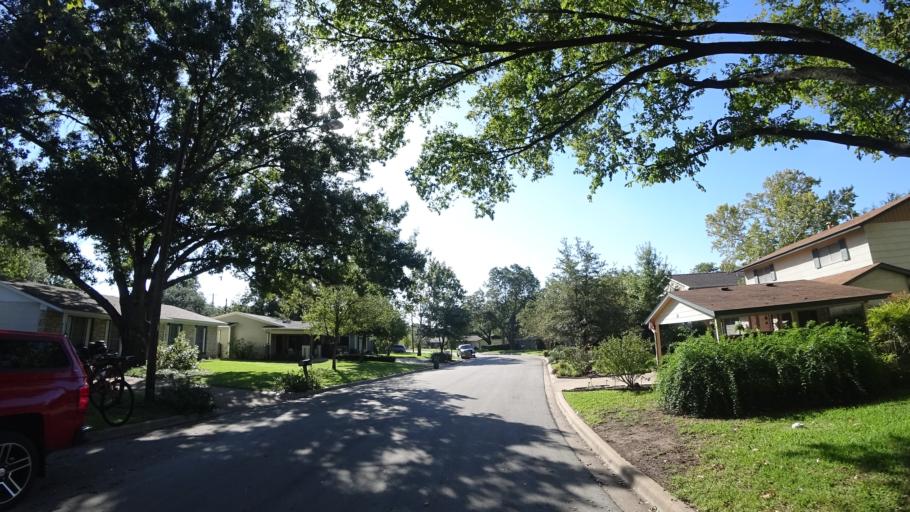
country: US
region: Texas
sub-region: Travis County
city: Austin
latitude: 30.3427
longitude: -97.7136
